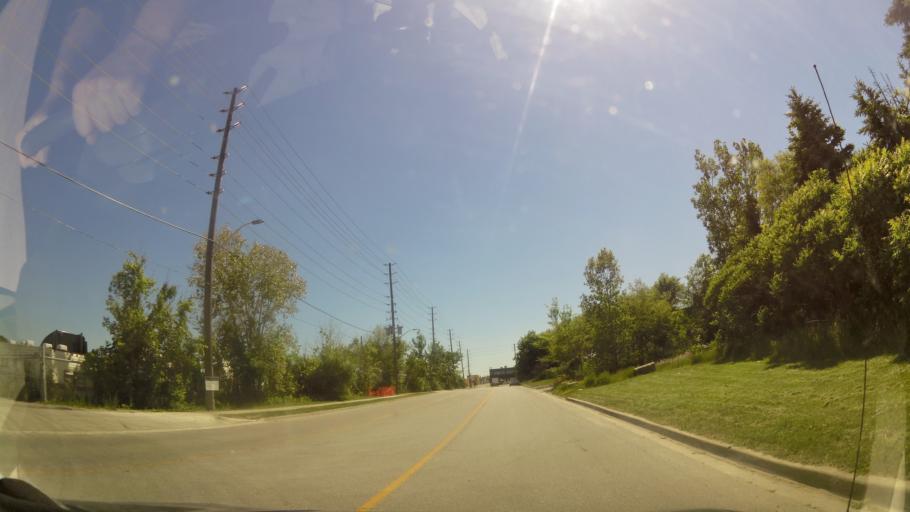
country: CA
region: Ontario
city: Etobicoke
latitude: 43.5949
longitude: -79.5896
